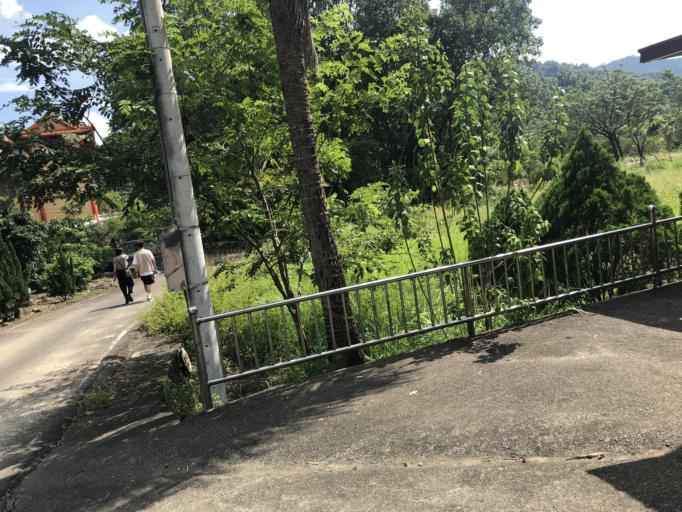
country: TW
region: Taiwan
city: Yujing
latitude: 22.9338
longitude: 120.5868
